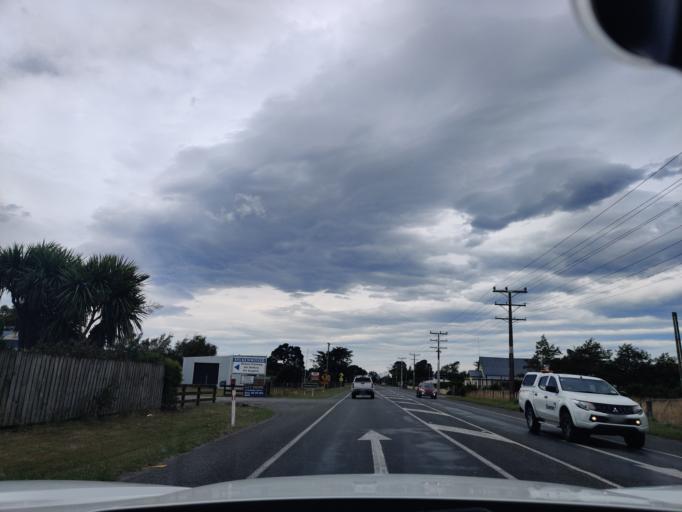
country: NZ
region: Wellington
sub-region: Masterton District
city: Masterton
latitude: -41.0114
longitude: 175.5443
